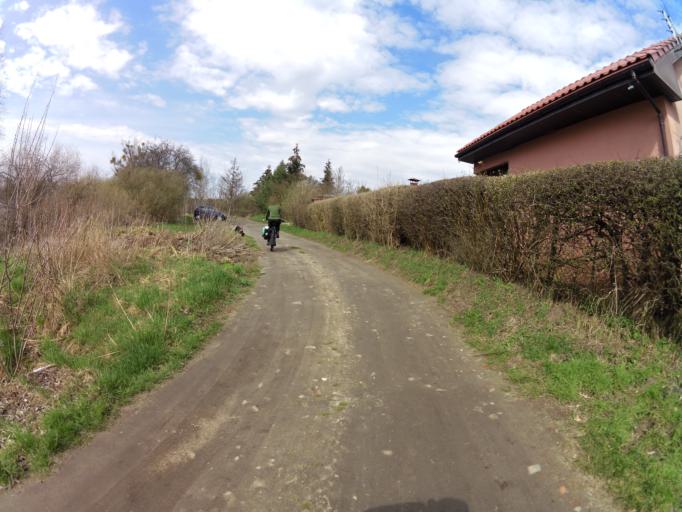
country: PL
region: West Pomeranian Voivodeship
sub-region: Powiat mysliborski
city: Mysliborz
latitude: 52.9354
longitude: 14.8600
